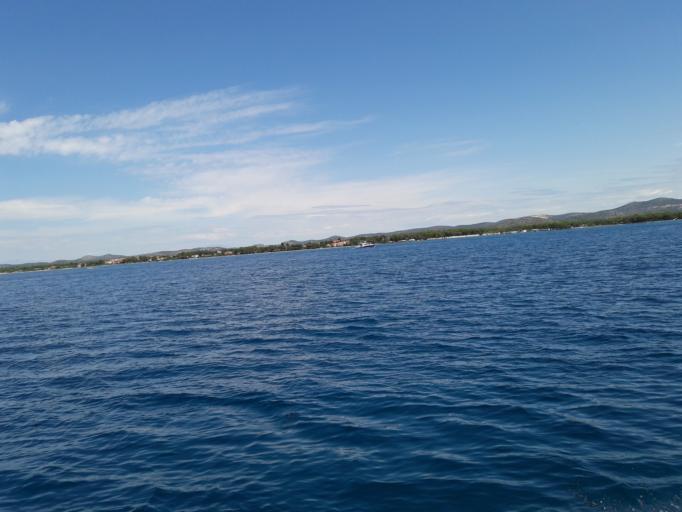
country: HR
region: Sibensko-Kniniska
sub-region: Grad Sibenik
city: Sibenik
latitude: 43.7151
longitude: 15.8404
